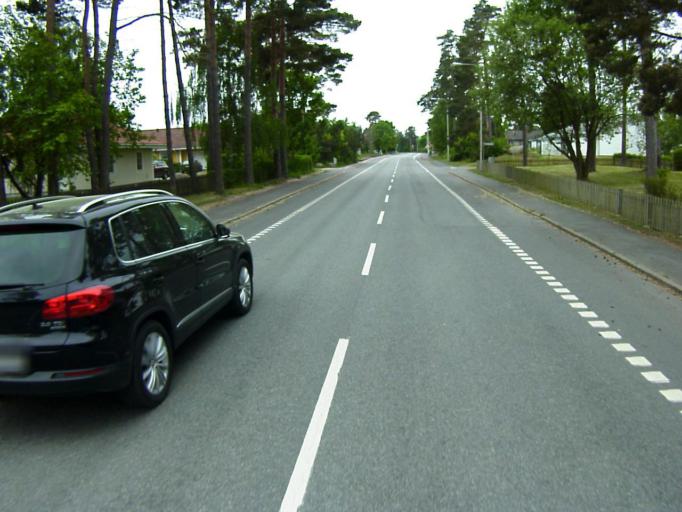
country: SE
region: Skane
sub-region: Kristianstads Kommun
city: Ahus
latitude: 55.9389
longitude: 14.2938
